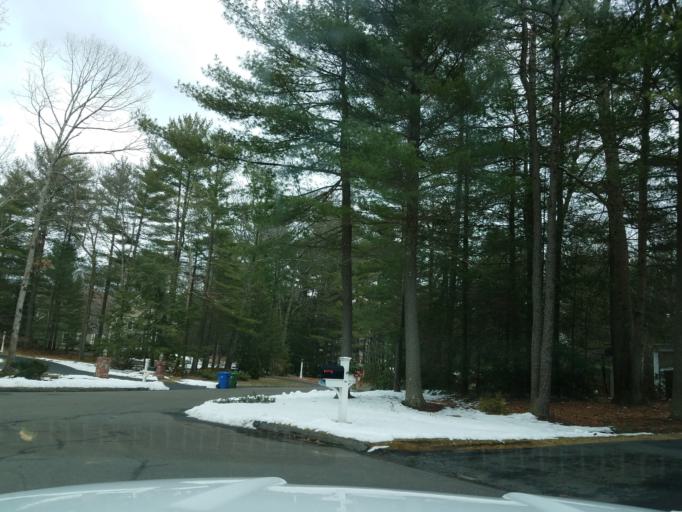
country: US
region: Connecticut
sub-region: Hartford County
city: Weatogue
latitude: 41.8058
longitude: -72.8520
